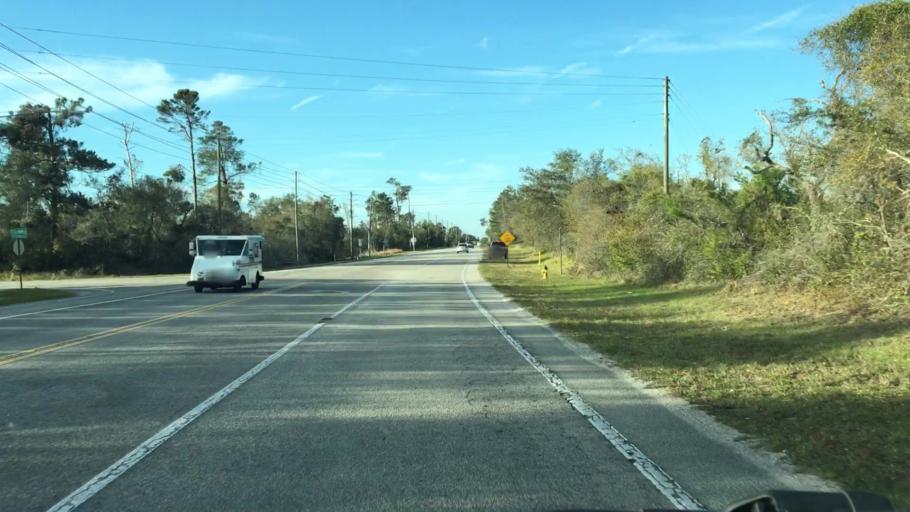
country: US
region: Florida
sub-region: Volusia County
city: Deltona
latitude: 28.9309
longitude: -81.2233
